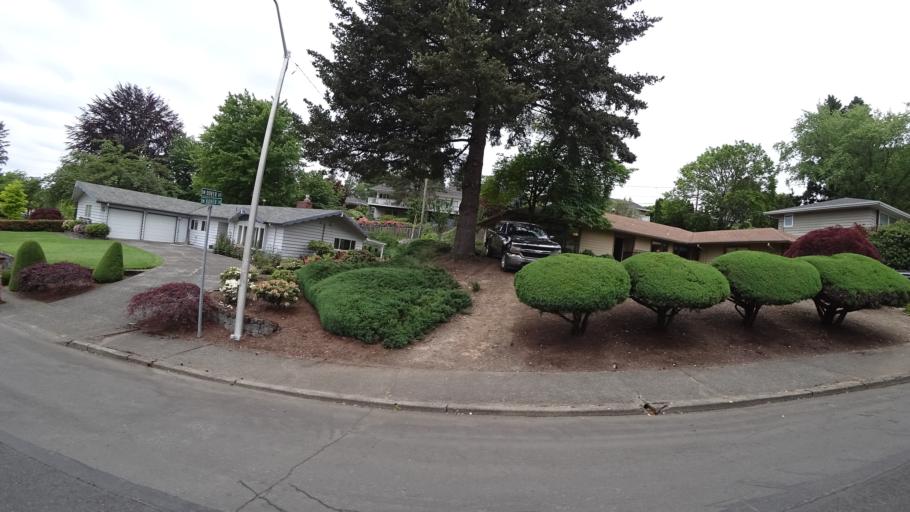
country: US
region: Oregon
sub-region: Washington County
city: Raleigh Hills
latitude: 45.4790
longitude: -122.7454
